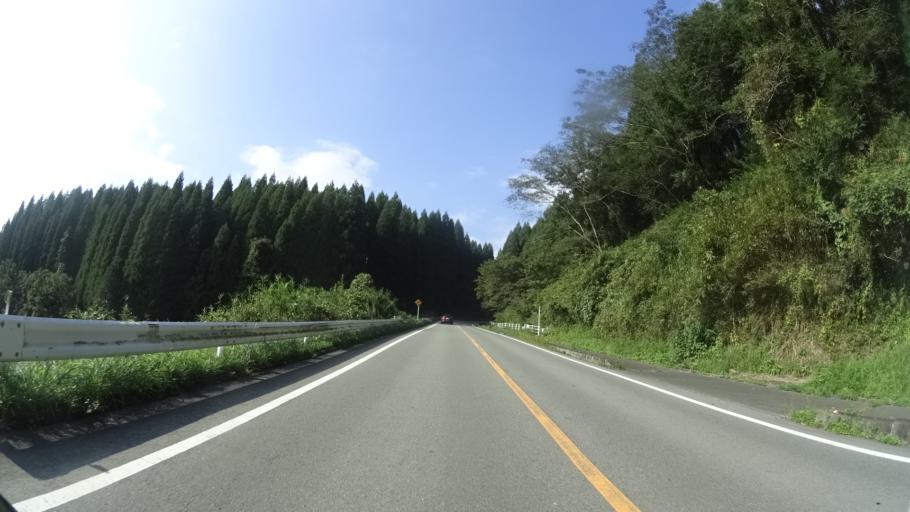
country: JP
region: Oita
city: Tsukawaki
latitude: 33.1323
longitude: 131.0872
